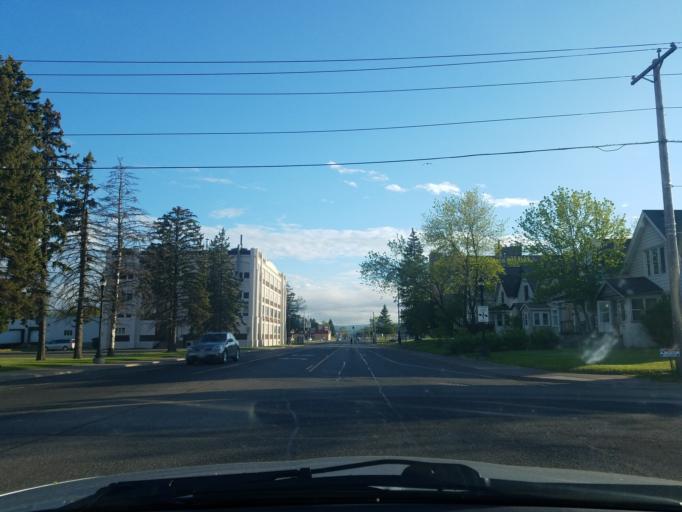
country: US
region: Wisconsin
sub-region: Douglas County
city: Superior
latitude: 46.7442
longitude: -92.1618
